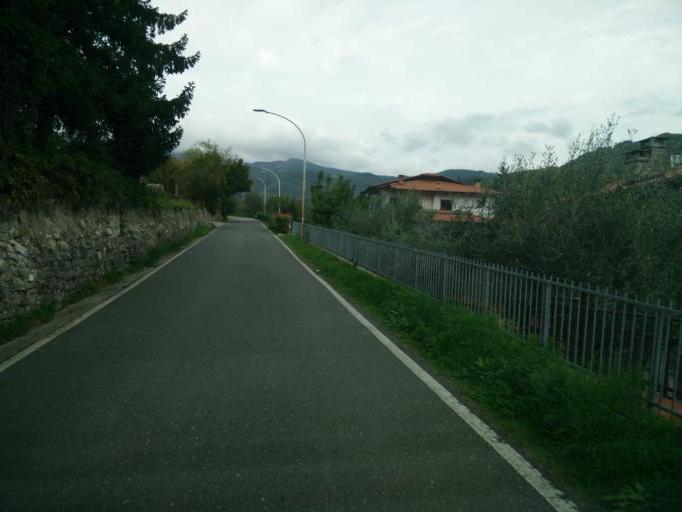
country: IT
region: Tuscany
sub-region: Provincia di Massa-Carrara
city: Casola in Lunigiana
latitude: 44.2115
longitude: 10.1859
